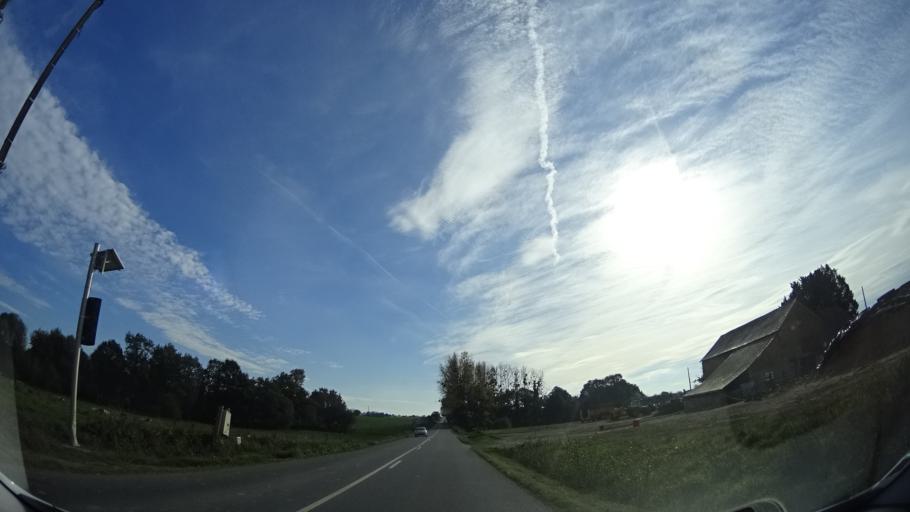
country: FR
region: Brittany
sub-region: Departement d'Ille-et-Vilaine
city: Bedee
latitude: 48.2076
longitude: -1.9414
